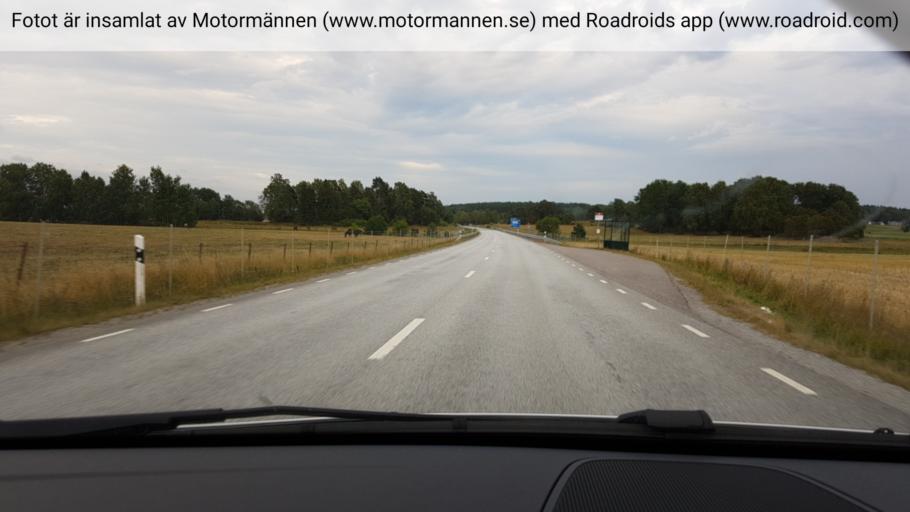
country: SE
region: Stockholm
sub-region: Upplands-Bro Kommun
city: Bro
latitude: 59.6012
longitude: 17.6107
